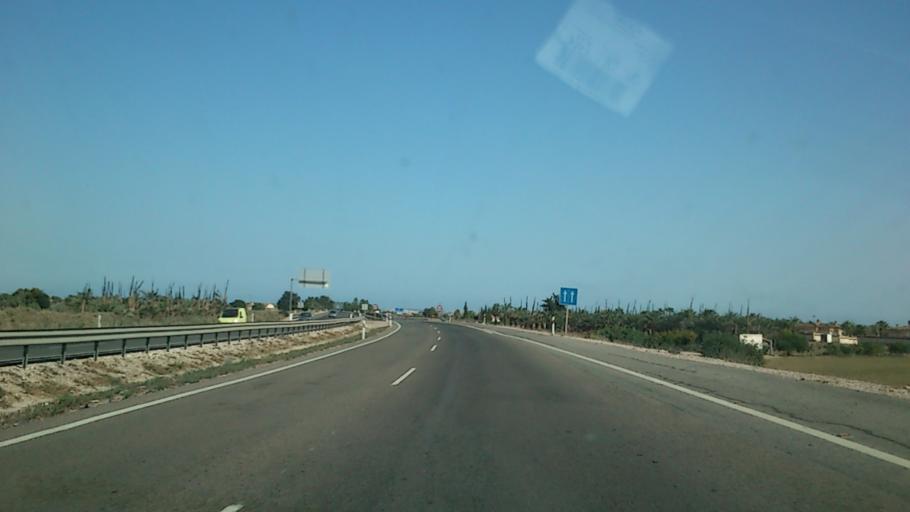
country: ES
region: Valencia
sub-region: Provincia de Alicante
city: Catral
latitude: 38.1450
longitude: -0.8164
